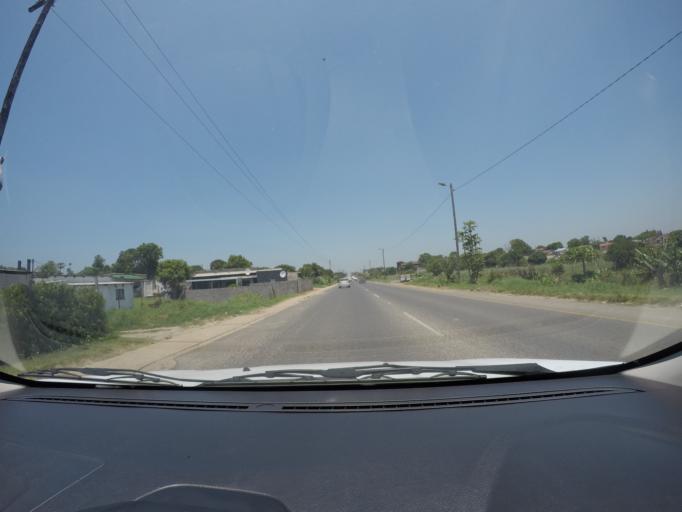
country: ZA
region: KwaZulu-Natal
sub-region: uThungulu District Municipality
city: eSikhawini
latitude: -28.8795
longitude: 31.9094
